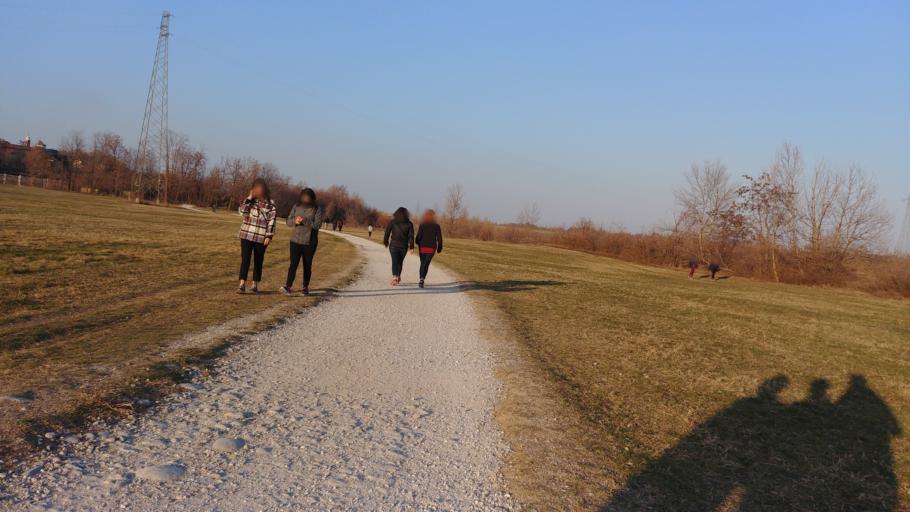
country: IT
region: Piedmont
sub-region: Provincia di Cuneo
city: Boves
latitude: 44.3584
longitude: 7.5342
